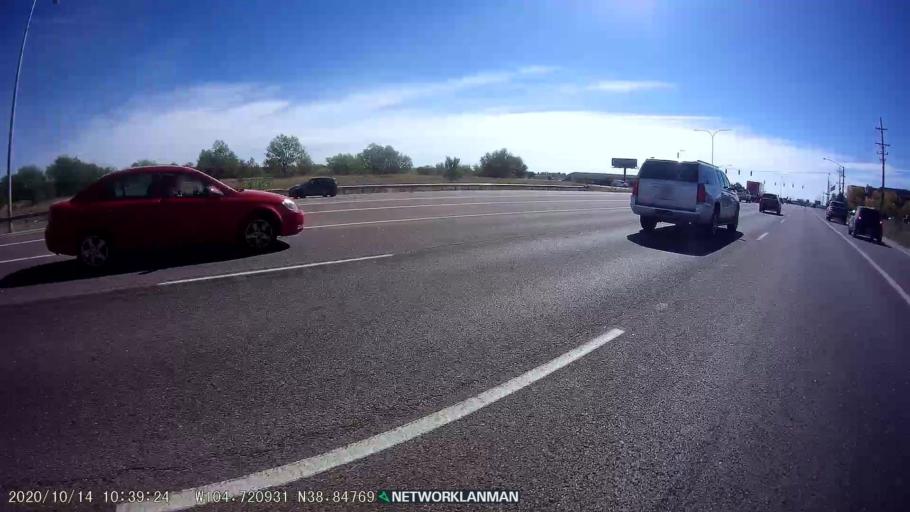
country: US
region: Colorado
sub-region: El Paso County
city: Cimarron Hills
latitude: 38.8475
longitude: -104.7211
